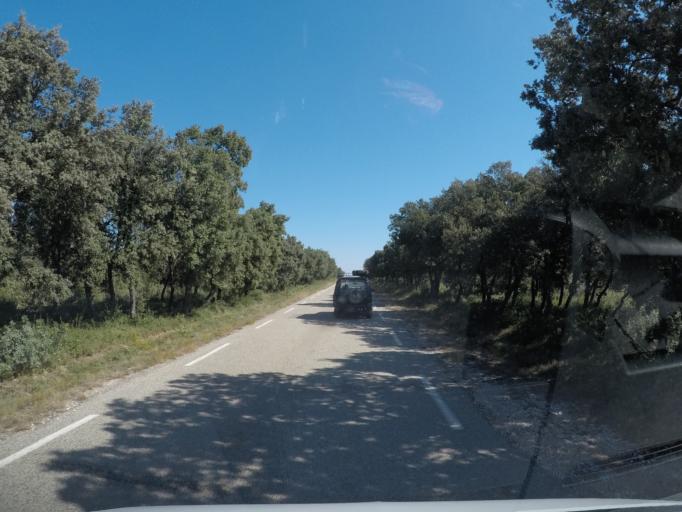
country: FR
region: Languedoc-Roussillon
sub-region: Departement du Gard
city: Saint-Victor-la-Coste
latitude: 44.0090
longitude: 4.6082
